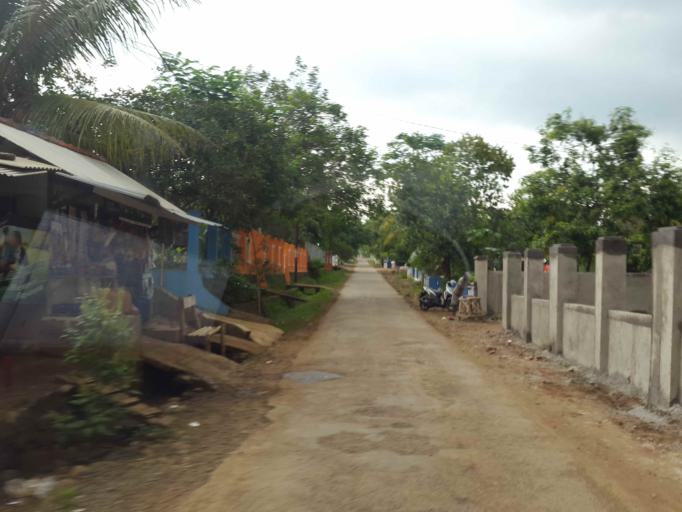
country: ID
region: Central Java
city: Limbangan
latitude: -7.3030
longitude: 108.7131
